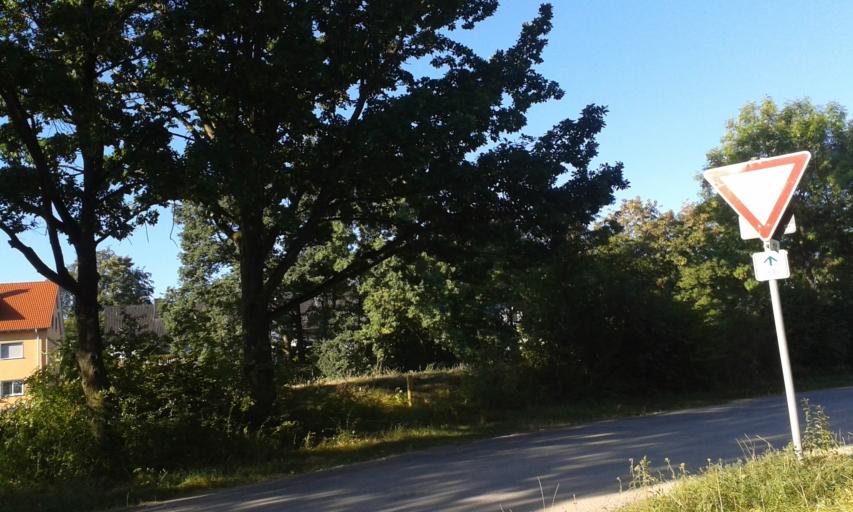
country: DE
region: Bavaria
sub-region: Upper Franconia
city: Bischberg
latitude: 49.9153
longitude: 10.8226
